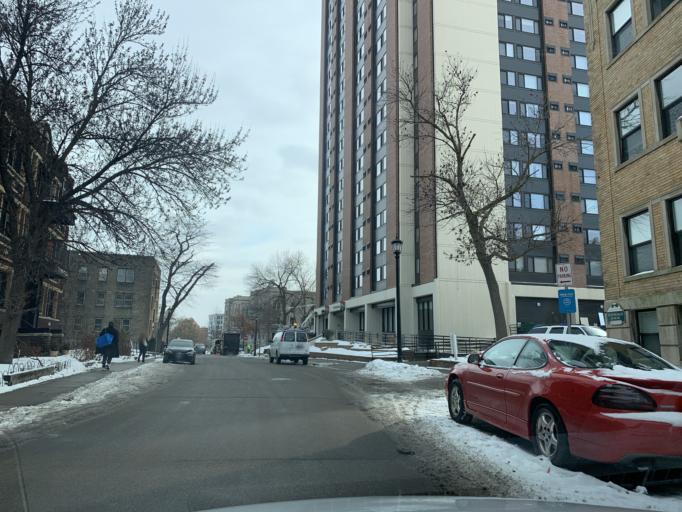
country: US
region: Minnesota
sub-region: Hennepin County
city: Minneapolis
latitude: 44.9666
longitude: -93.2821
